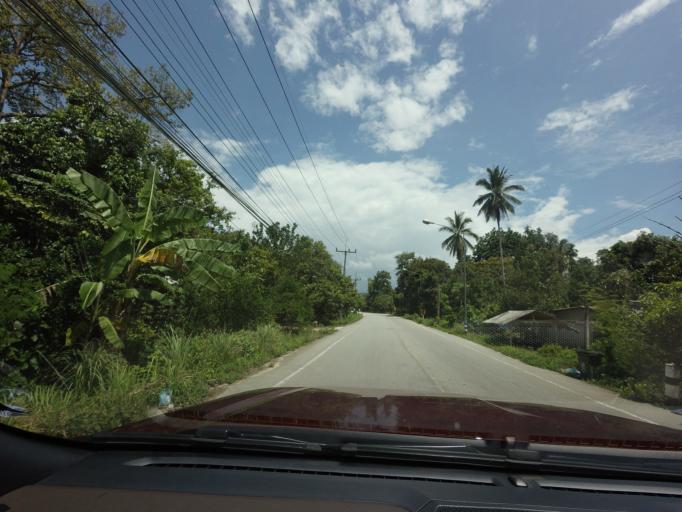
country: TH
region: Narathiwat
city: Chanae
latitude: 6.0956
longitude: 101.6914
